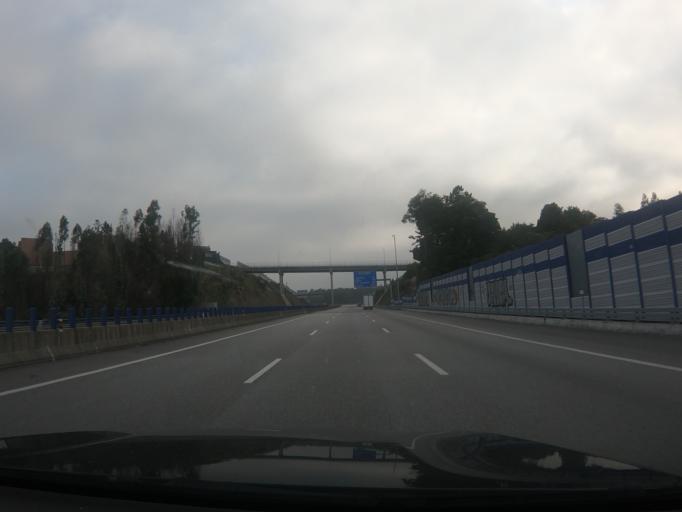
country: PT
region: Porto
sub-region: Vila Nova de Gaia
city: Sandim
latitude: 41.0603
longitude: -8.4619
